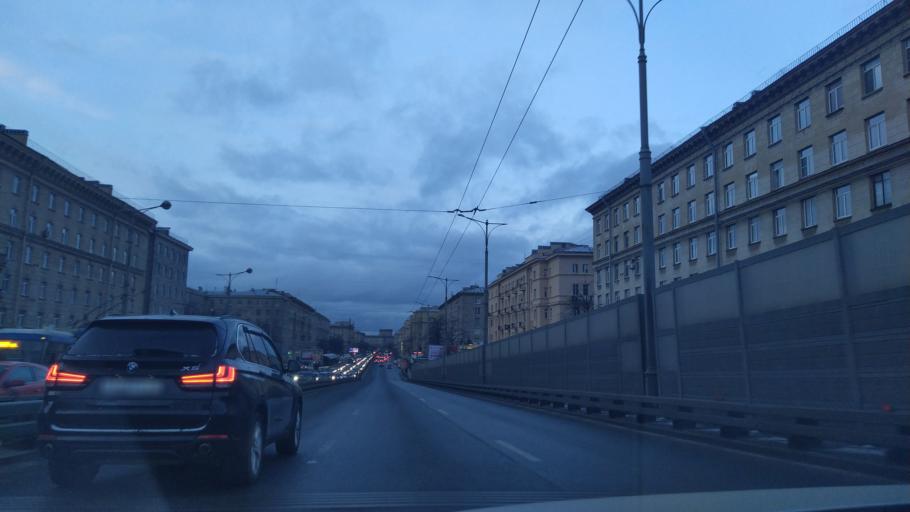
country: RU
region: St.-Petersburg
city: Avtovo
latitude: 59.8656
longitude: 30.2612
